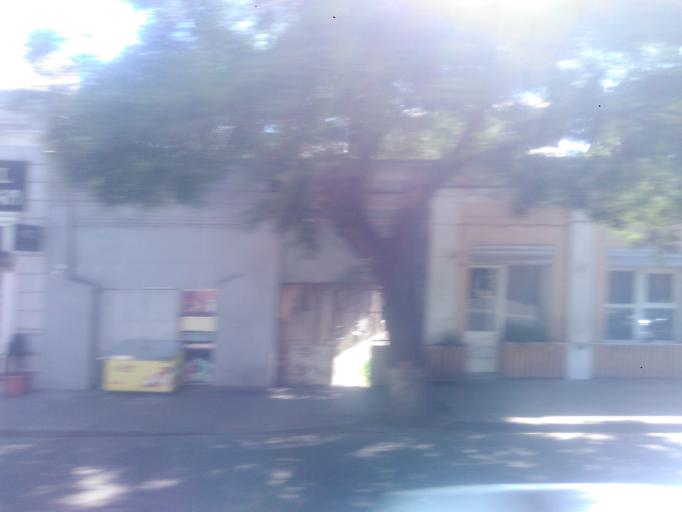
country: GE
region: T'bilisi
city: Tbilisi
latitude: 41.6912
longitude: 44.8162
